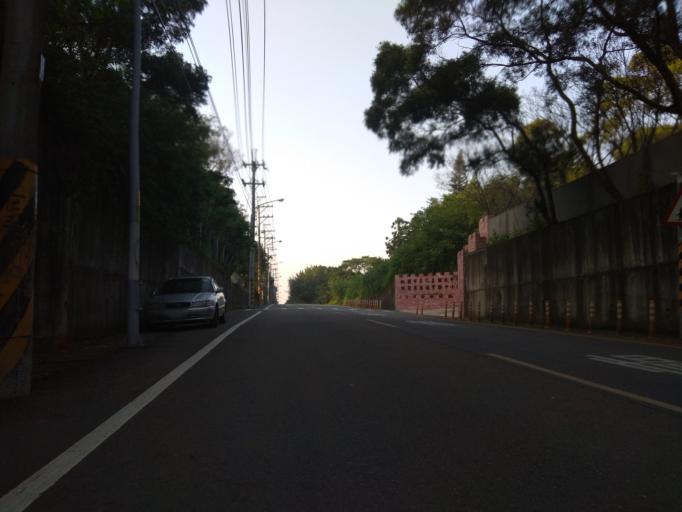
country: TW
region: Taiwan
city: Daxi
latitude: 24.9246
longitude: 121.1827
